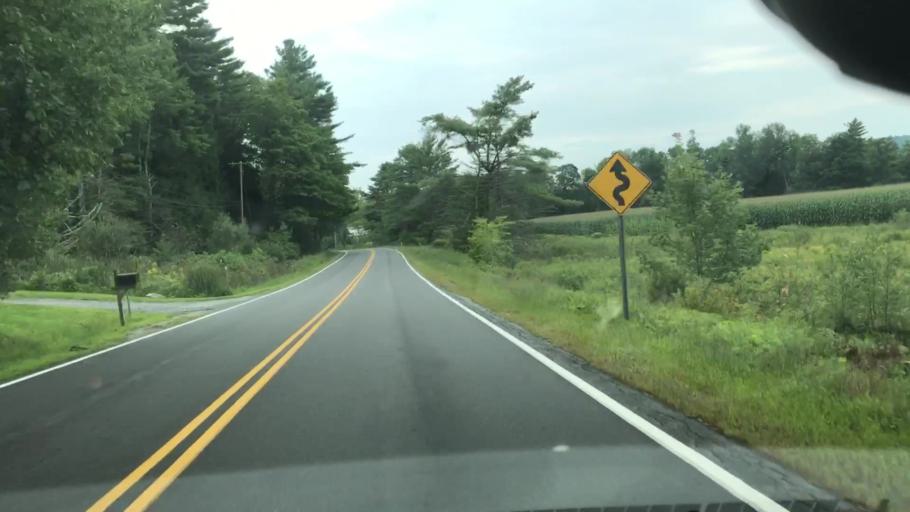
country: US
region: New Hampshire
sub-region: Grafton County
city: Woodsville
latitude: 44.2350
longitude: -72.0440
